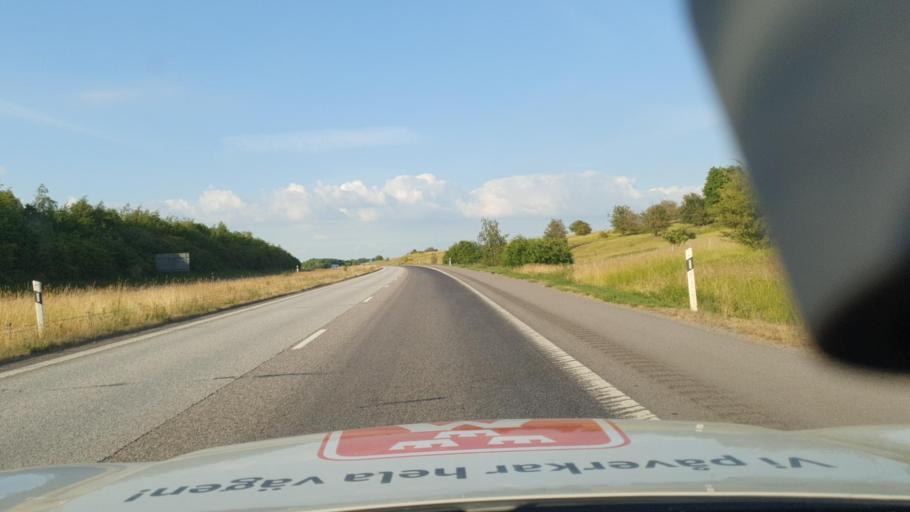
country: SE
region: Skane
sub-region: Malmo
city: Oxie
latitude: 55.5707
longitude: 13.0999
